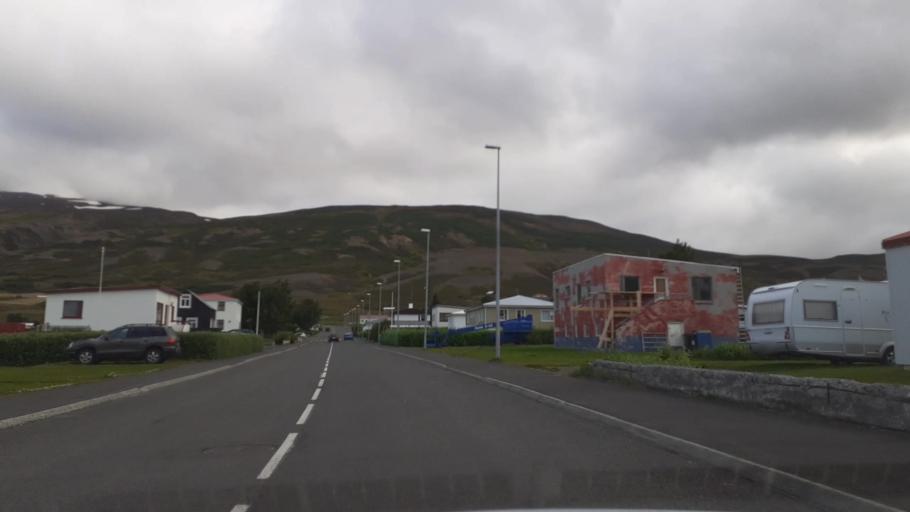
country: IS
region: Northeast
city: Akureyri
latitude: 65.9483
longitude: -18.1825
